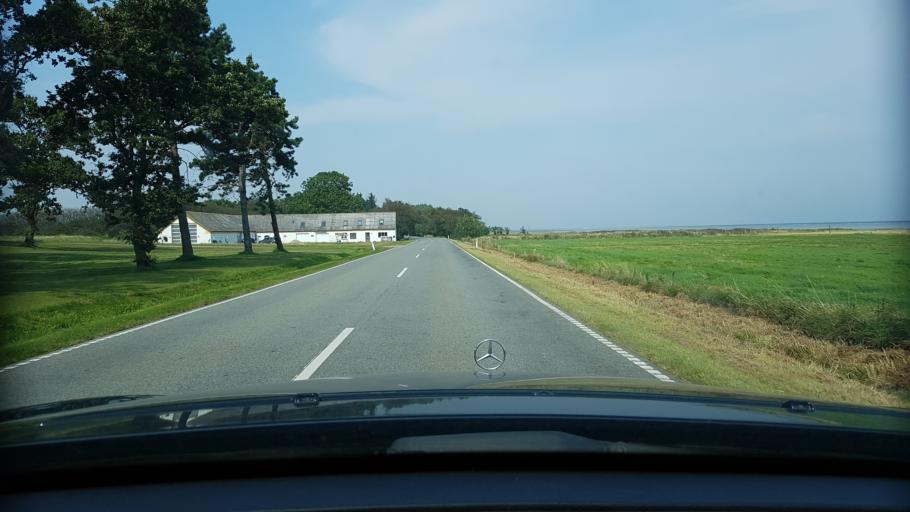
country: DK
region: North Denmark
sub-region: Alborg Kommune
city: Hals
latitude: 56.8857
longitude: 10.2616
